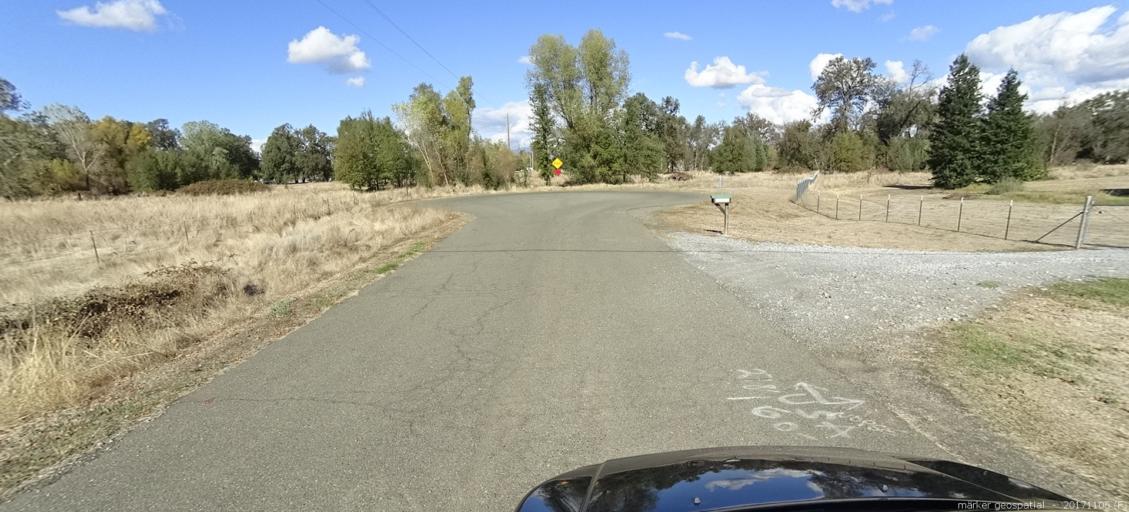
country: US
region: California
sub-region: Shasta County
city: Palo Cedro
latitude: 40.5985
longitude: -122.2299
